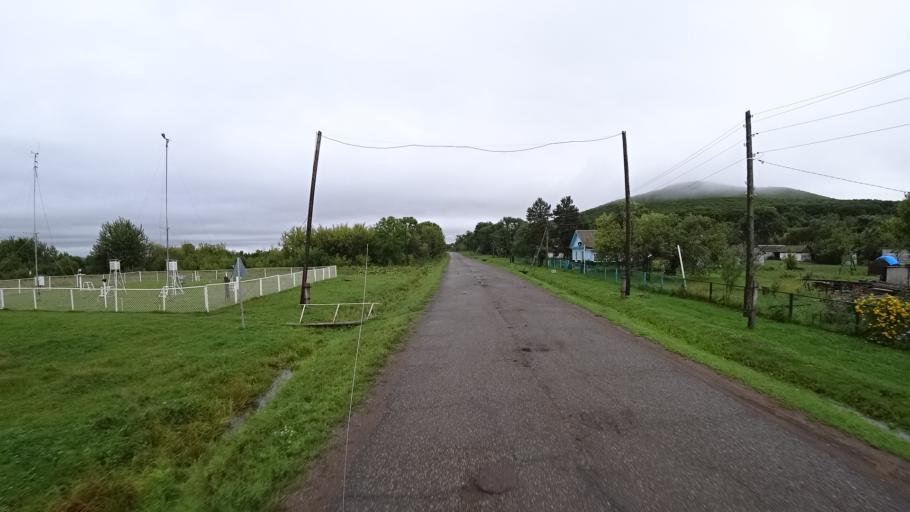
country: RU
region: Primorskiy
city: Monastyrishche
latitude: 44.2703
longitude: 132.4205
